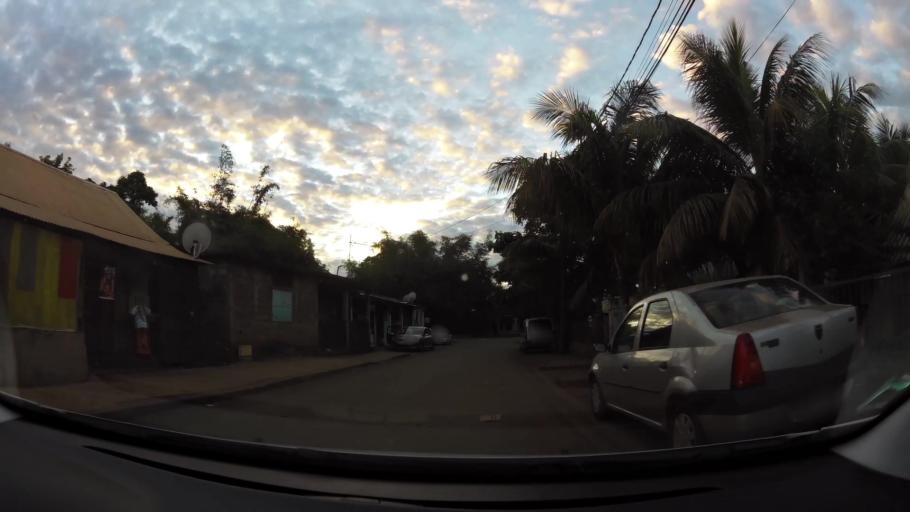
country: YT
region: Koungou
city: Koungou
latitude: -12.7333
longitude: 45.1619
